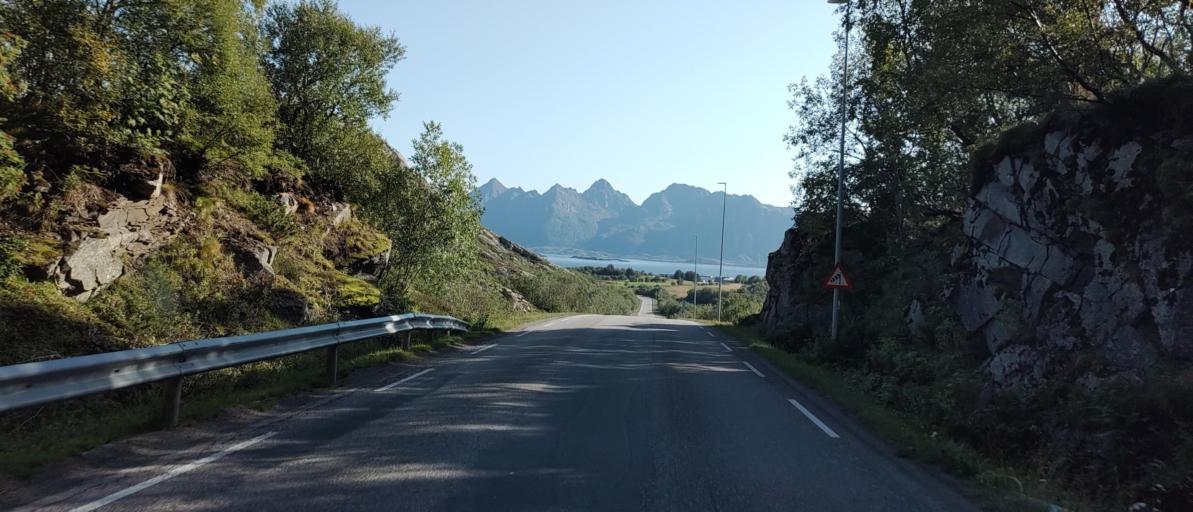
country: NO
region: Nordland
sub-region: Vagan
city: Svolvaer
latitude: 68.2431
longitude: 14.6359
